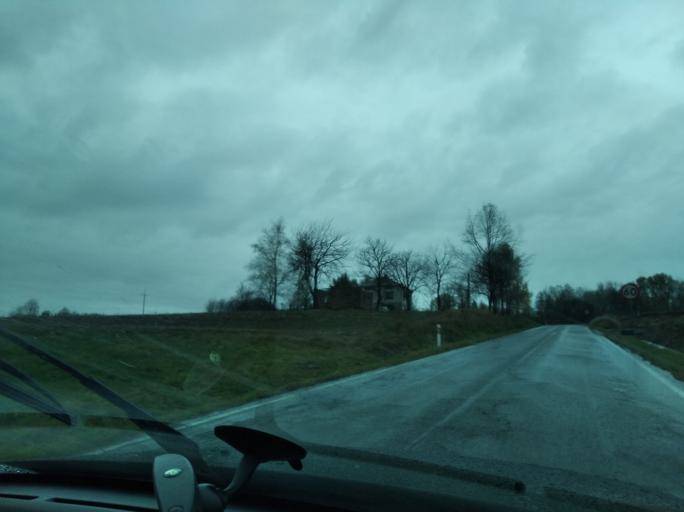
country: PL
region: Subcarpathian Voivodeship
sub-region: Powiat lancucki
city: Handzlowka
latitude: 49.9837
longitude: 22.1923
